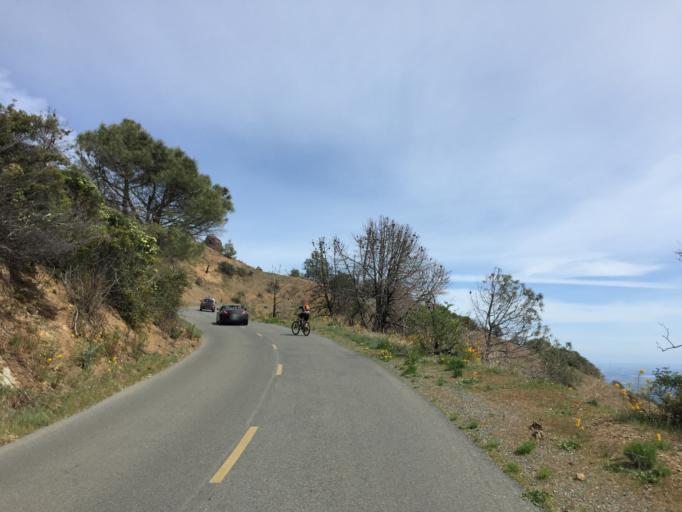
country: US
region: California
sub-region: Contra Costa County
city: Blackhawk
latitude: 37.8791
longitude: -121.9160
